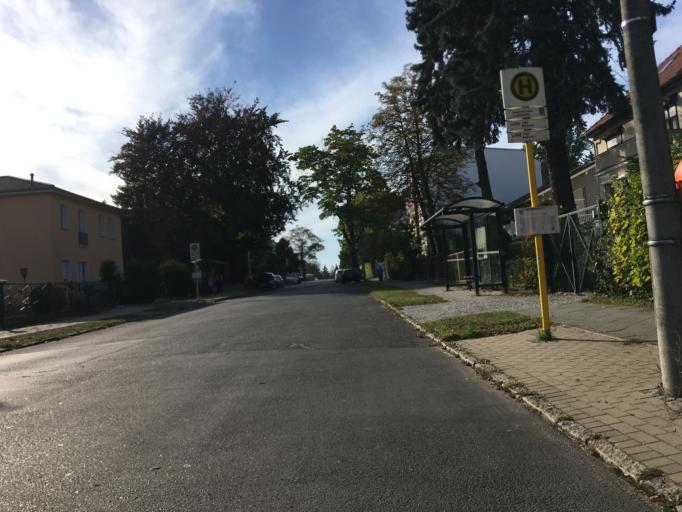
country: DE
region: Berlin
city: Mahlsdorf
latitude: 52.5123
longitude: 13.6196
